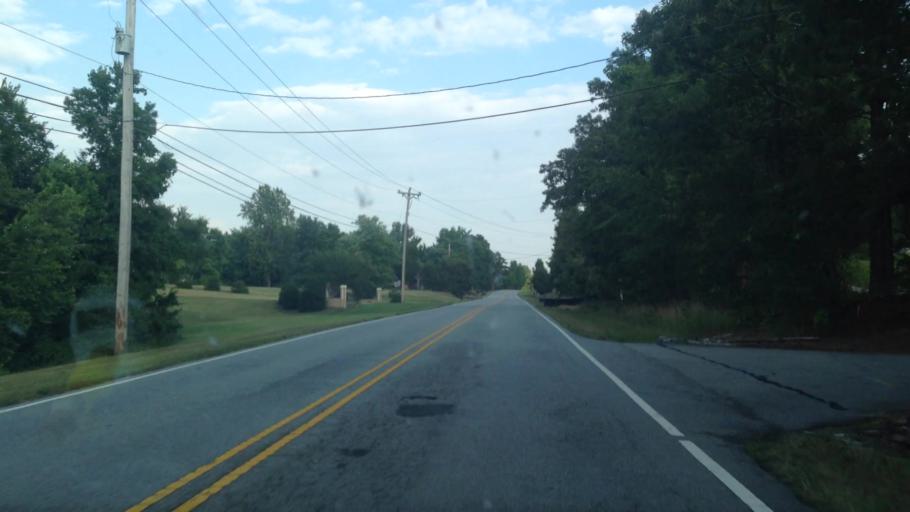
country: US
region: North Carolina
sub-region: Guilford County
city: High Point
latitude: 35.9620
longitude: -80.0765
